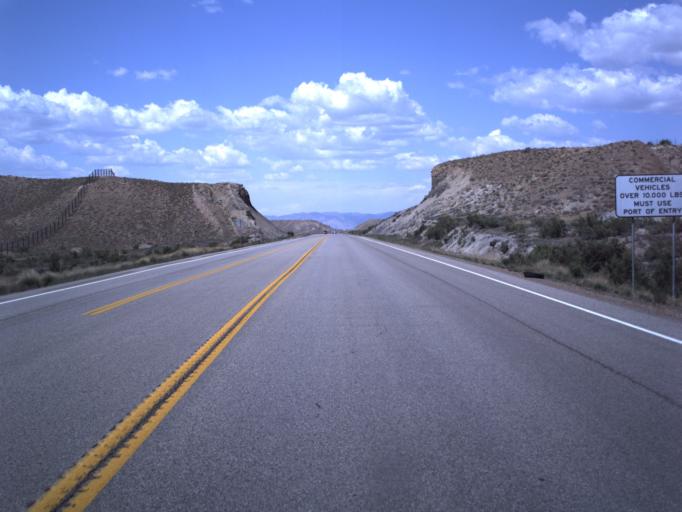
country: US
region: Utah
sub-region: Emery County
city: Huntington
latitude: 39.4433
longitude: -110.8647
